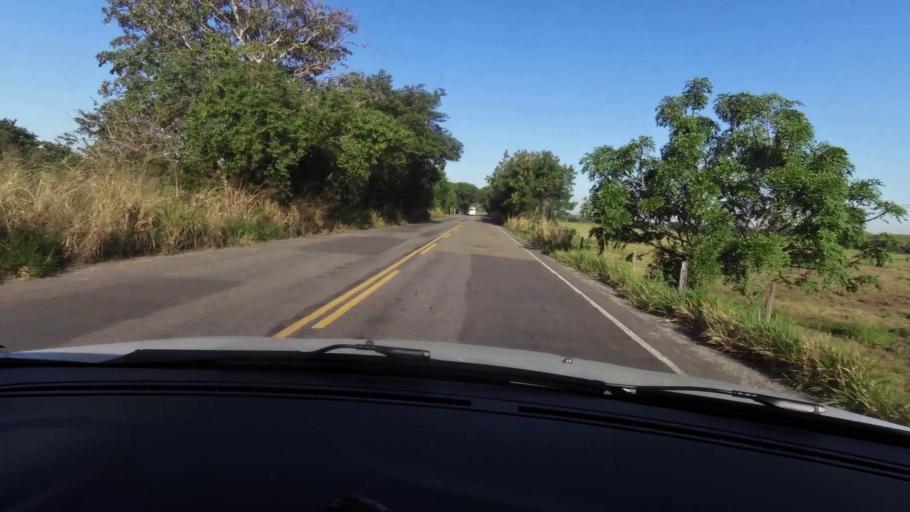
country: BR
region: Espirito Santo
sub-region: Alfredo Chaves
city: Alfredo Chaves
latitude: -20.7133
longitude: -40.6676
